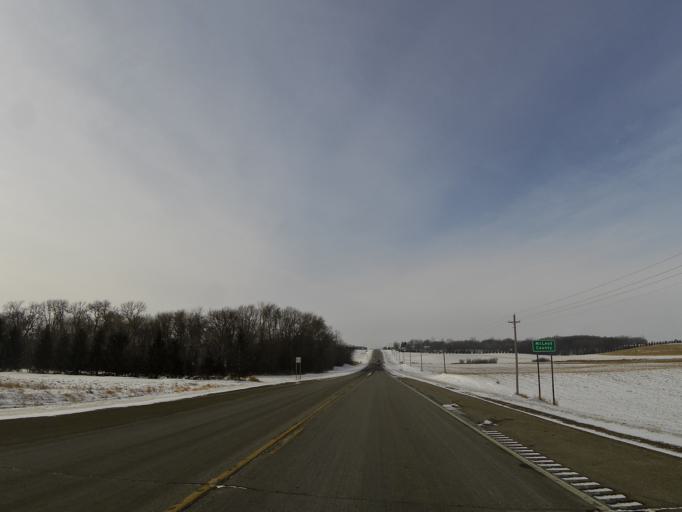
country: US
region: Minnesota
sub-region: McLeod County
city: Lester Prairie
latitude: 44.9061
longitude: -94.0130
